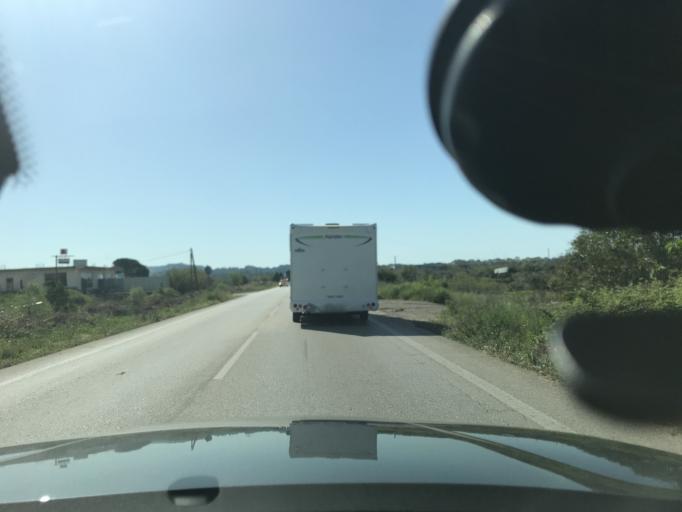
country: GR
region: West Greece
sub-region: Nomos Ileias
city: Pyrgos
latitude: 37.6550
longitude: 21.4669
